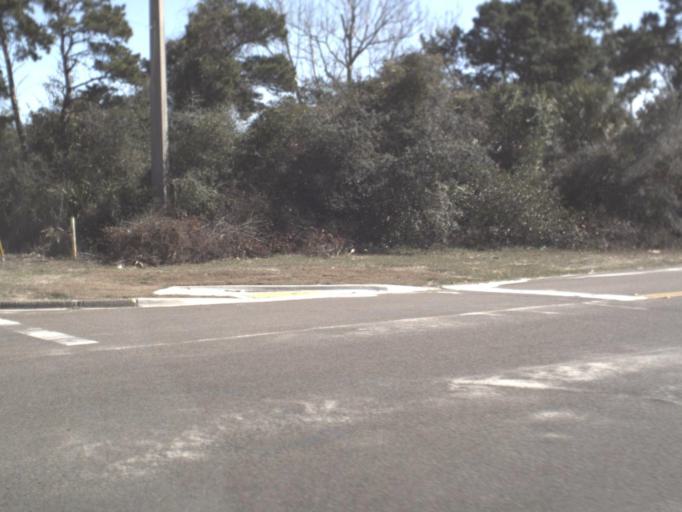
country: US
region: Florida
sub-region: Bay County
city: Panama City Beach
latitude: 30.1986
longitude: -85.8363
